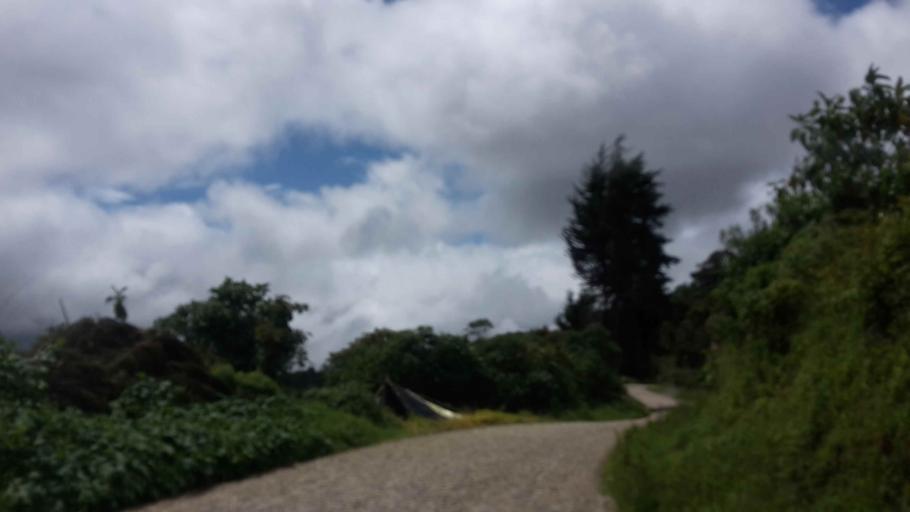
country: BO
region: Cochabamba
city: Colomi
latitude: -17.1428
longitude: -65.9195
